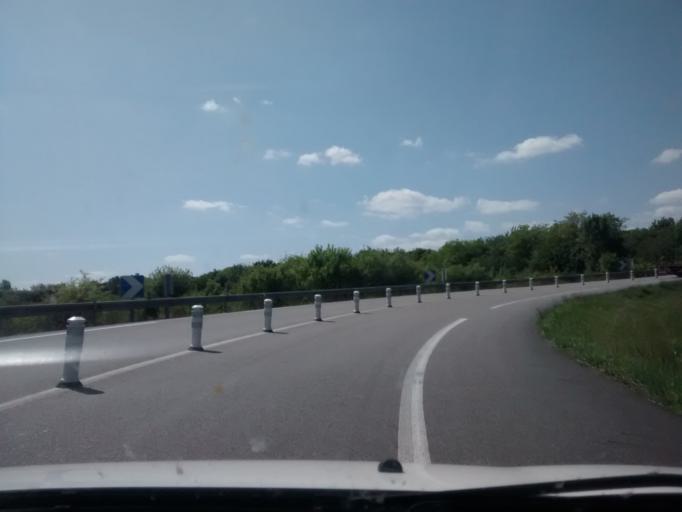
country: FR
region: Ile-de-France
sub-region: Departement des Yvelines
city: Ablis
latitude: 48.5251
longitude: 1.8350
